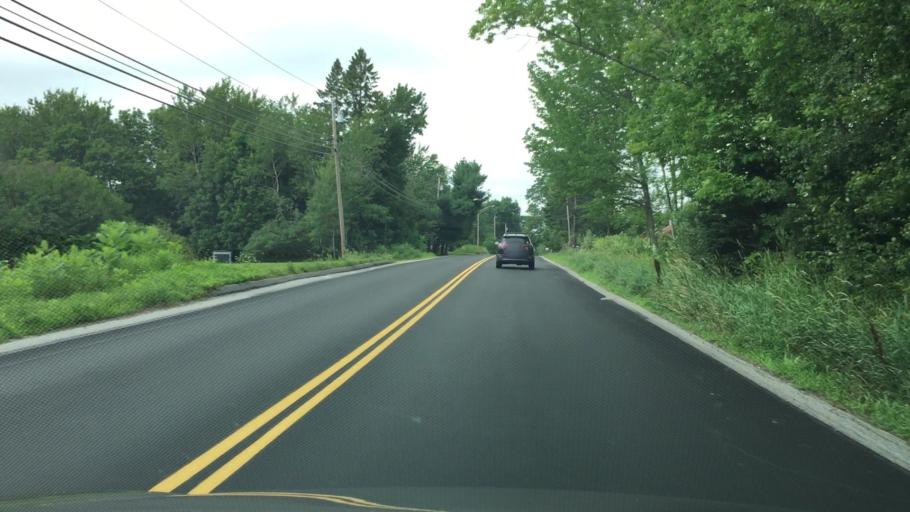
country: US
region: Maine
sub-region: Waldo County
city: Winterport
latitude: 44.6238
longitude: -68.8326
